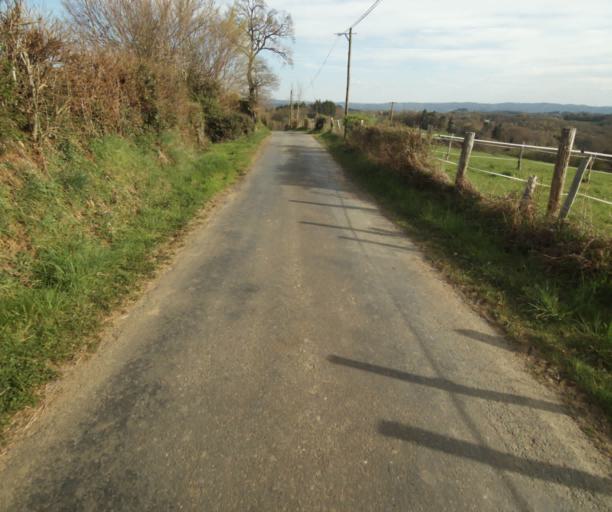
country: FR
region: Limousin
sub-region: Departement de la Correze
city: Naves
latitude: 45.3225
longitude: 1.7426
